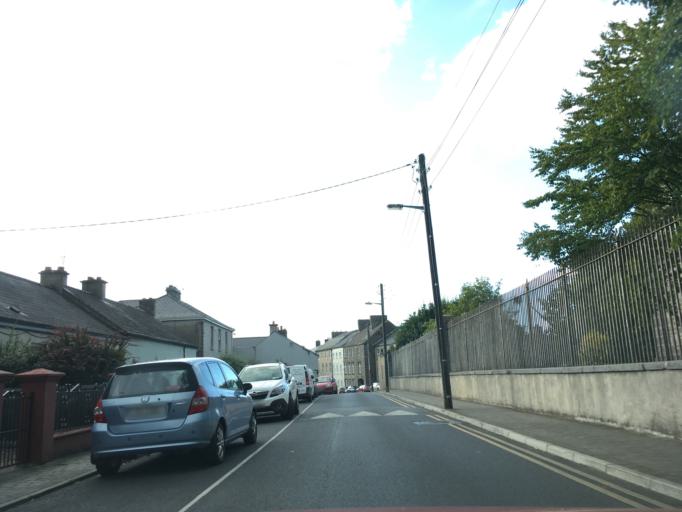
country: IE
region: Munster
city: Cashel
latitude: 52.5149
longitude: -7.8858
